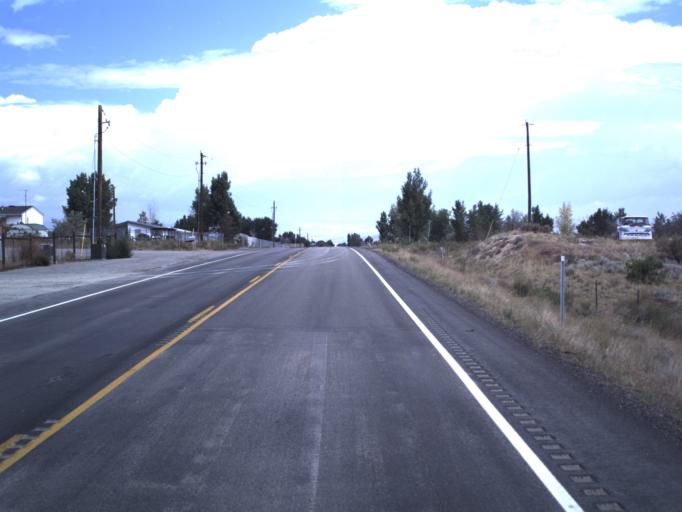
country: US
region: Utah
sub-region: Uintah County
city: Naples
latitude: 40.3673
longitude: -109.4983
